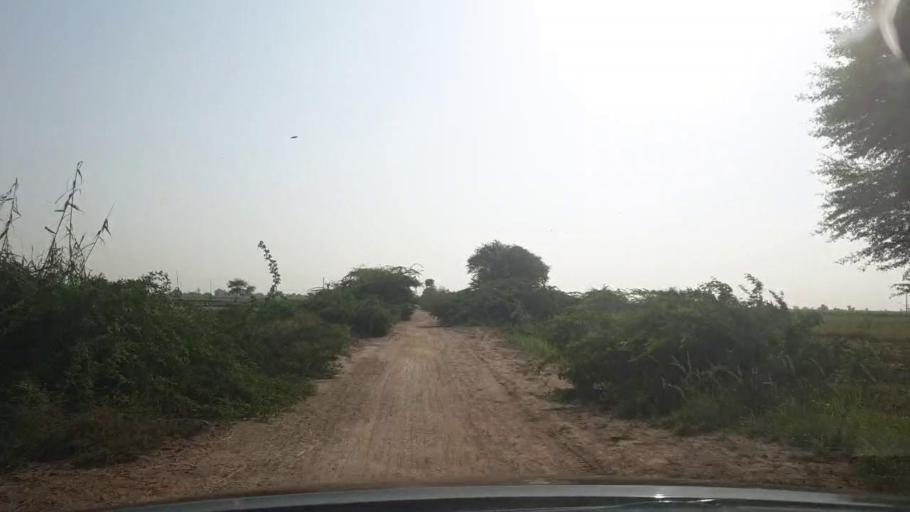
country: PK
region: Sindh
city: Tando Bago
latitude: 24.6509
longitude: 69.1610
